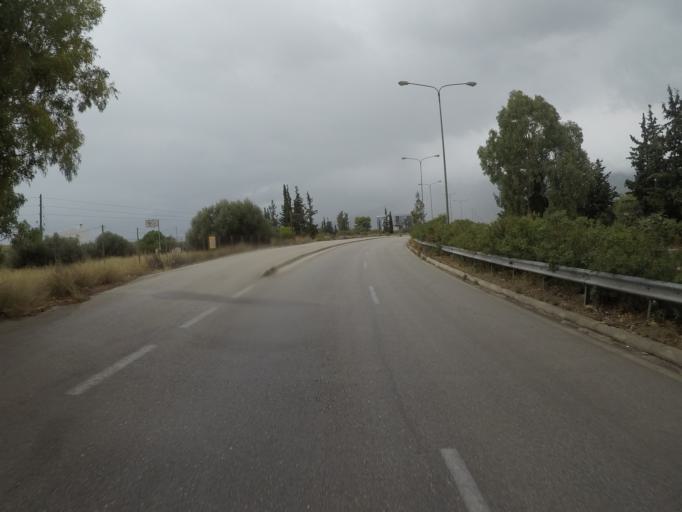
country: GR
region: Peloponnese
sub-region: Nomos Korinthias
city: Korinthos
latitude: 37.9405
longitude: 22.9791
